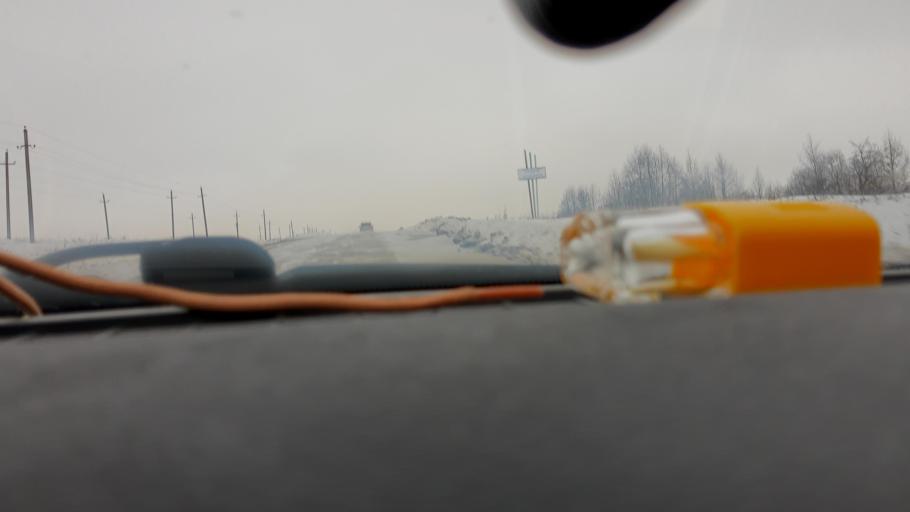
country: RU
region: Bashkortostan
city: Ulukulevo
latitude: 54.5246
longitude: 56.4259
